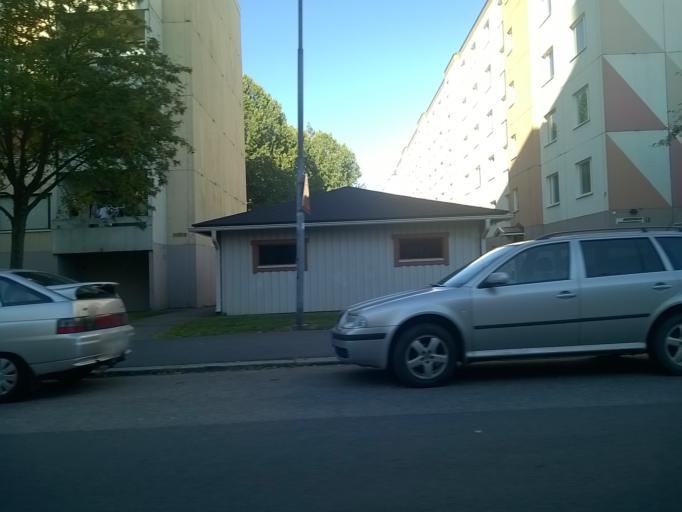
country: FI
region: Pirkanmaa
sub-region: Tampere
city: Tampere
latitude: 61.4527
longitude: 23.8368
